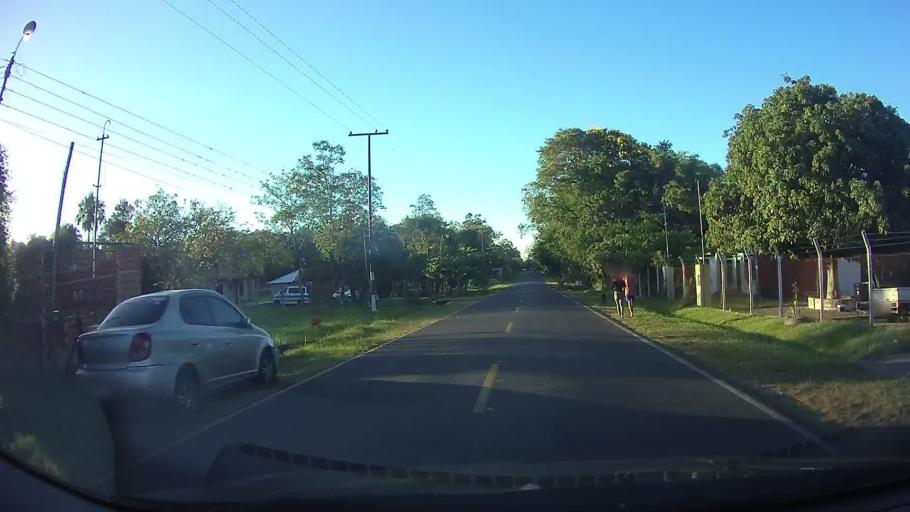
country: PY
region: Central
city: Aregua
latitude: -25.2746
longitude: -57.4079
